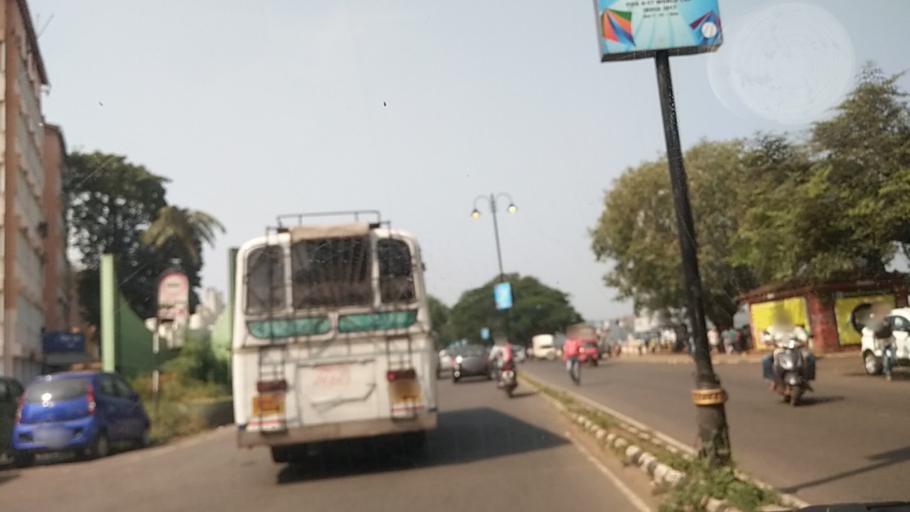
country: IN
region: Goa
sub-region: North Goa
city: Panaji
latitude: 15.5011
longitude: 73.8260
